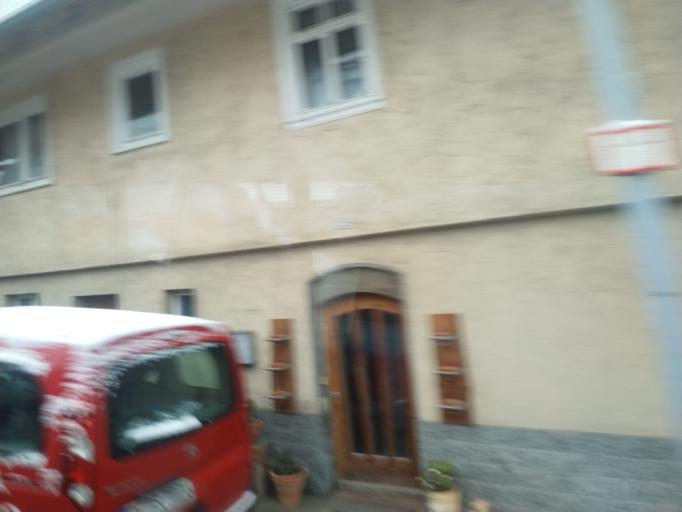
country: DE
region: Baden-Wuerttemberg
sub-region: Karlsruhe Region
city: Neuenburg
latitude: 48.8598
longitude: 8.5670
